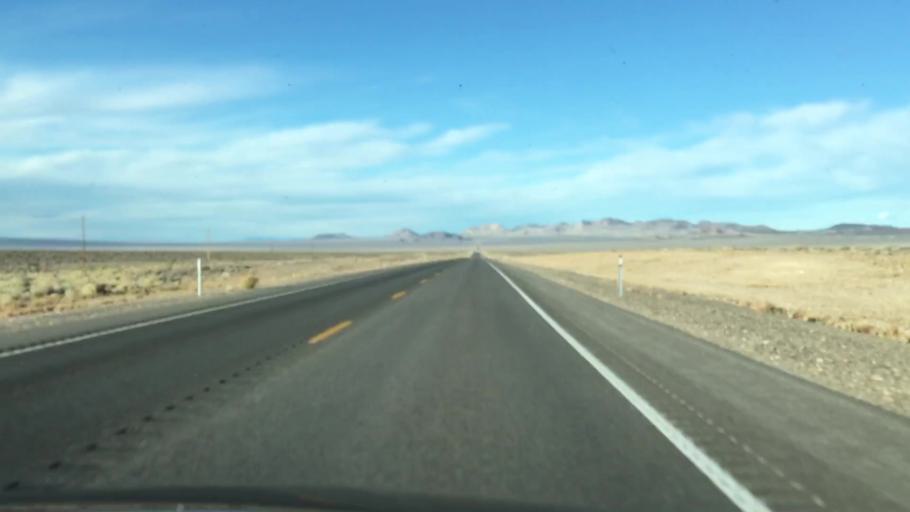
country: US
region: Nevada
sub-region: Esmeralda County
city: Goldfield
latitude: 37.8060
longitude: -117.2396
